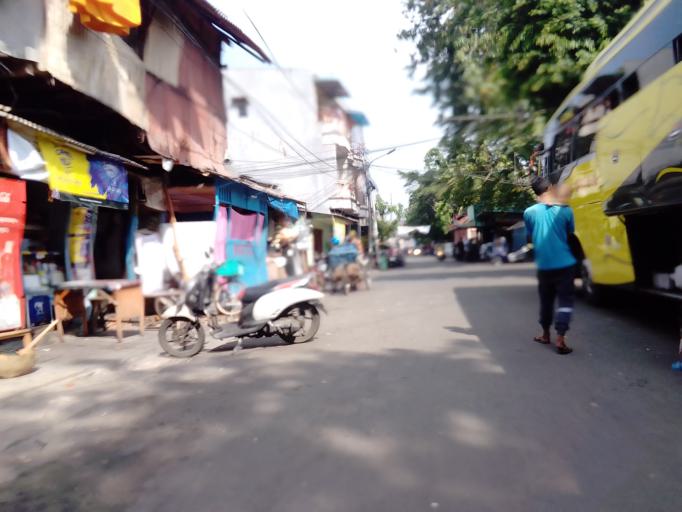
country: ID
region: Jakarta Raya
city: Jakarta
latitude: -6.1470
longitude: 106.8115
